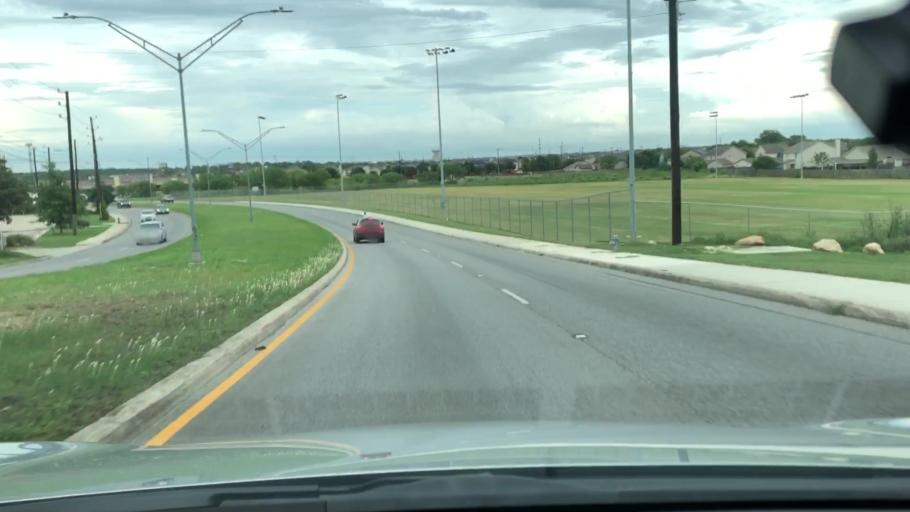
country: US
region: Texas
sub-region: Bexar County
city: Leon Valley
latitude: 29.4763
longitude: -98.6662
